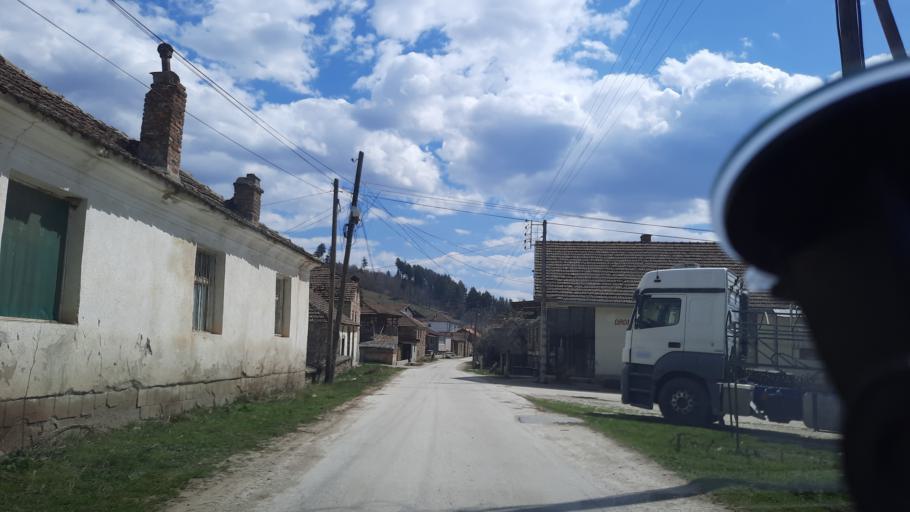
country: MK
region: Demir Hisar
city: Sopotnica
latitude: 41.2973
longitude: 21.1530
